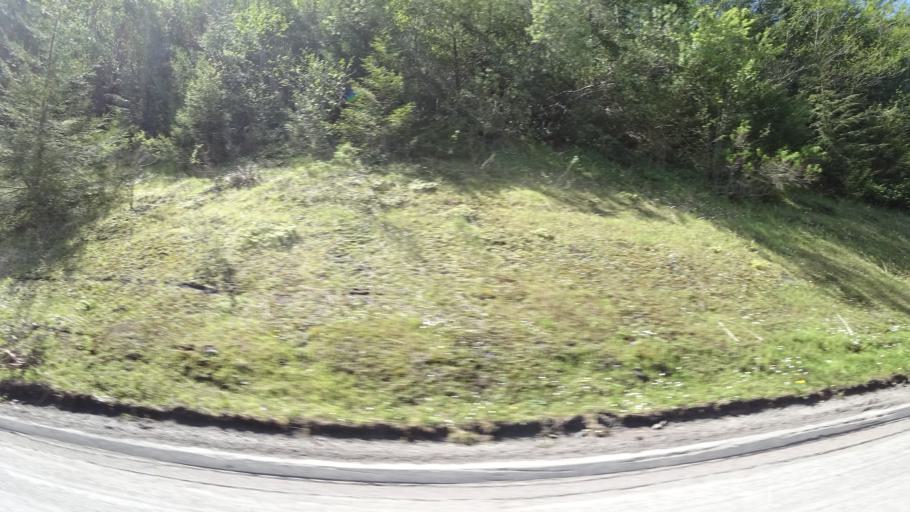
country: US
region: California
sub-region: Del Norte County
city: Bertsch-Oceanview
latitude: 41.4247
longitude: -124.0046
